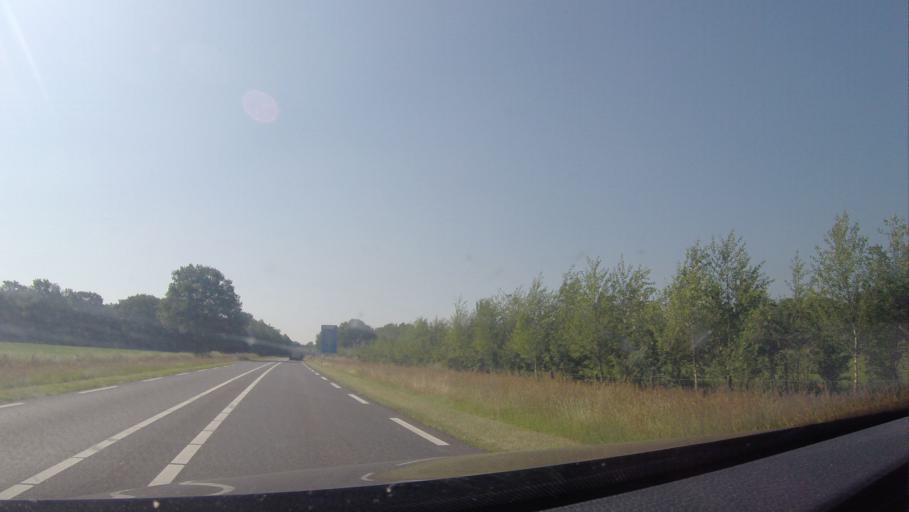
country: NL
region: Gelderland
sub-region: Gemeente Lochem
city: Laren
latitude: 52.2883
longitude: 6.3964
